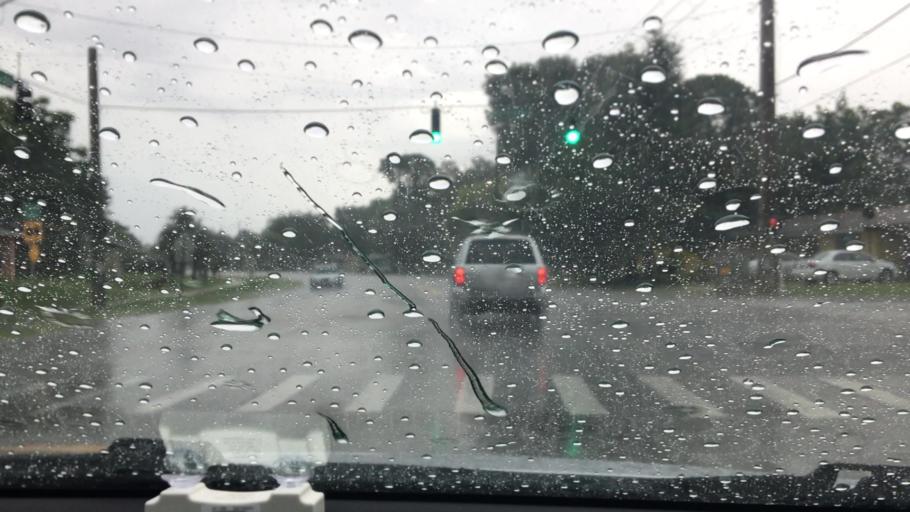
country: US
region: Florida
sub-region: Volusia County
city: Deltona
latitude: 28.9010
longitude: -81.2635
